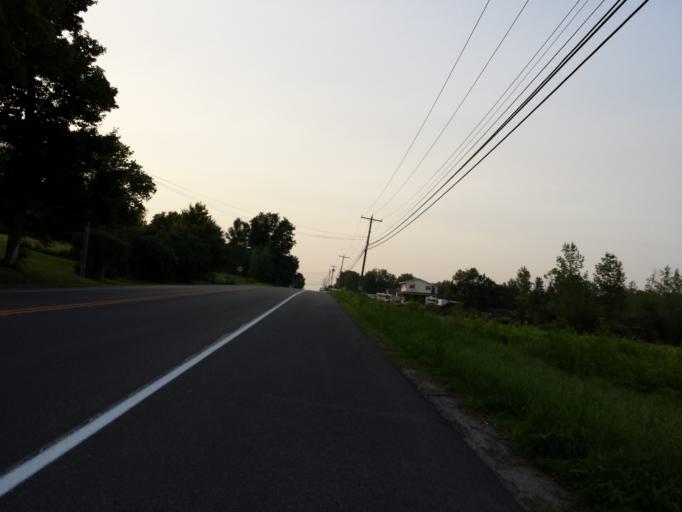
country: US
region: New York
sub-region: St. Lawrence County
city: Potsdam
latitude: 44.7070
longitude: -74.9871
